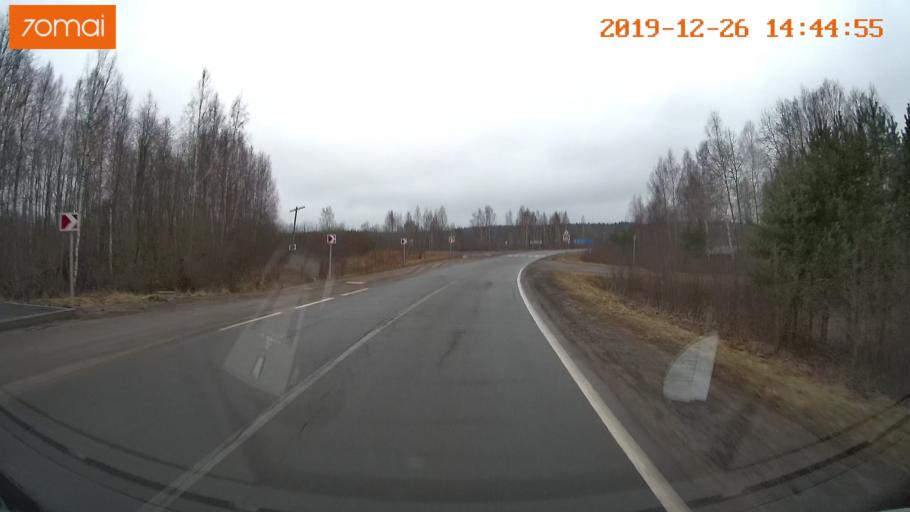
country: RU
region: Jaroslavl
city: Poshekhon'ye
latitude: 58.3418
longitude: 39.0495
